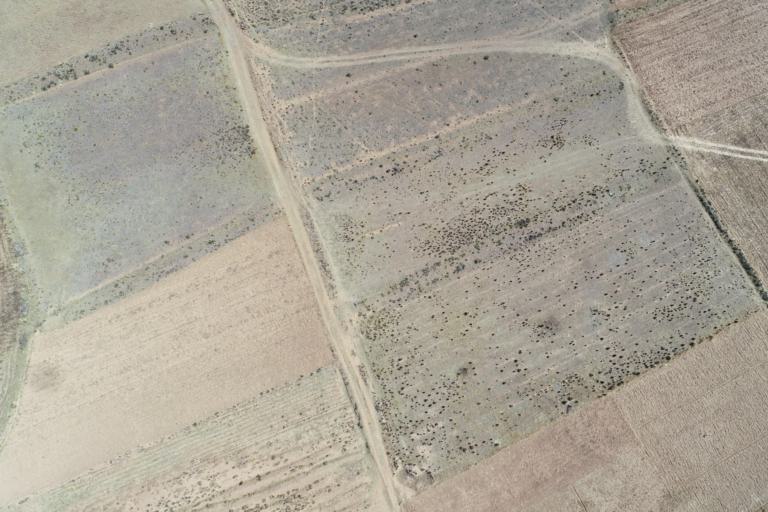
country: BO
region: La Paz
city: Achacachi
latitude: -15.9002
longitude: -68.8987
